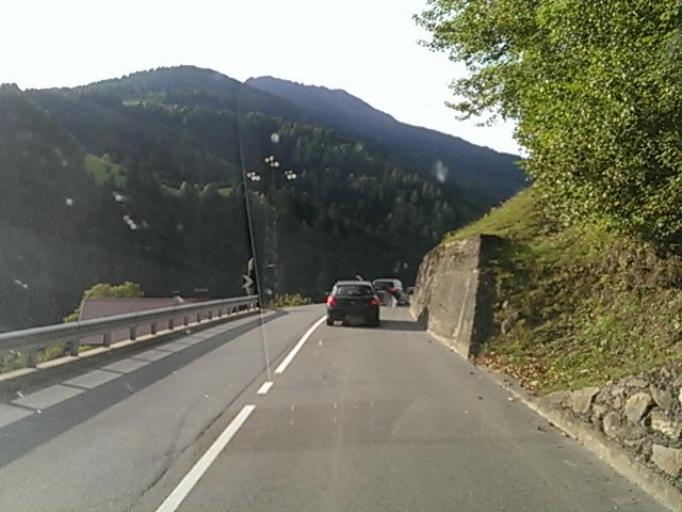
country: IT
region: Trentino-Alto Adige
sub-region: Bolzano
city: San Pancrazio
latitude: 46.5702
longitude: 11.0694
